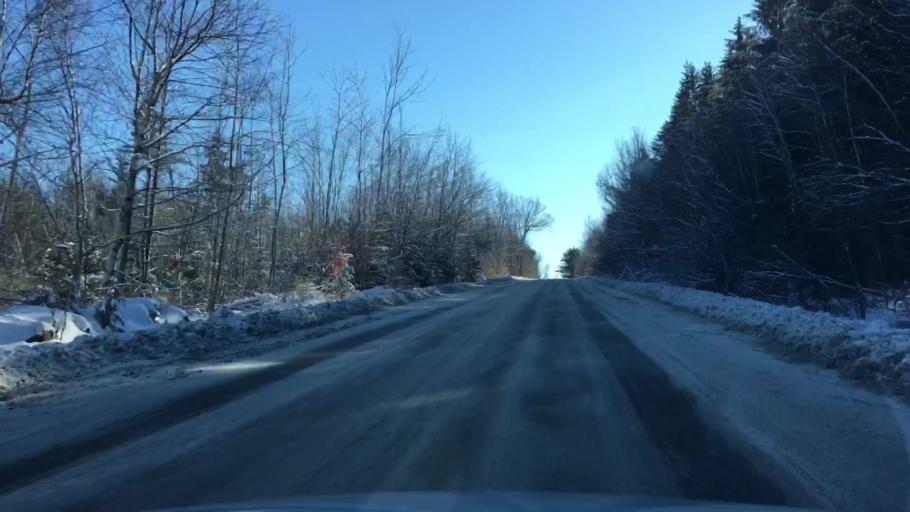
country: US
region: Maine
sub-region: Kennebec County
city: Winthrop
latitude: 44.3479
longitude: -69.9901
